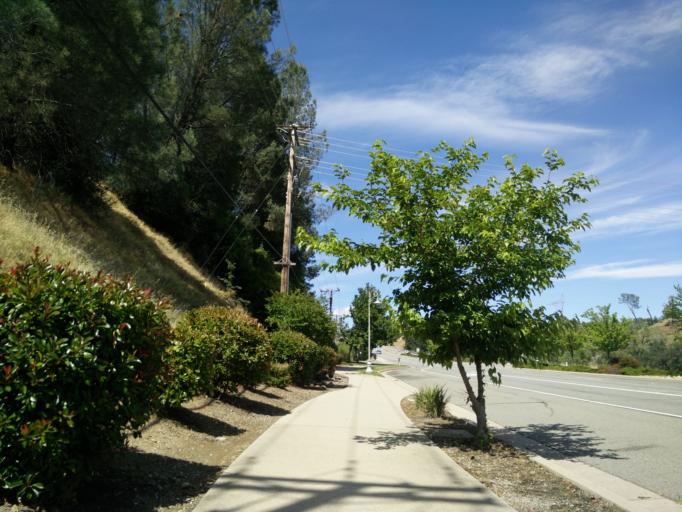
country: US
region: California
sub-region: Shasta County
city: Redding
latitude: 40.6000
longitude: -122.3839
